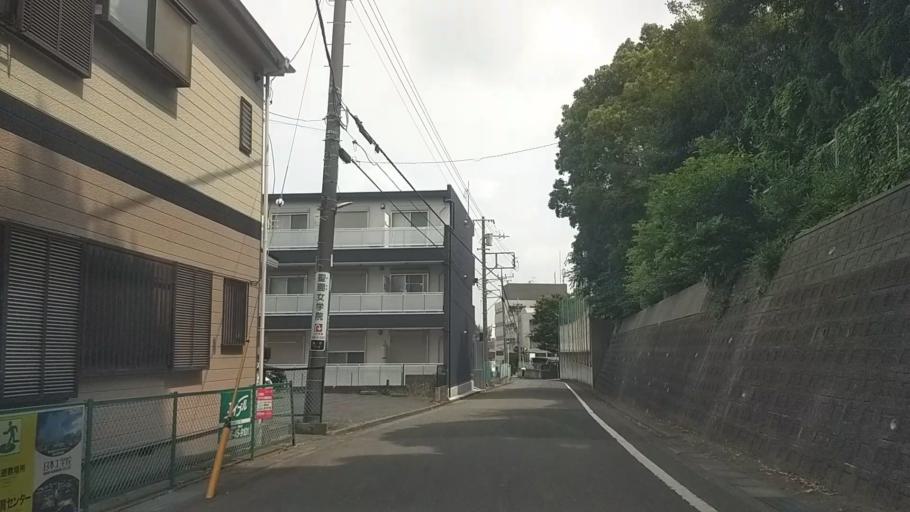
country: JP
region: Kanagawa
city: Fujisawa
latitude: 35.3612
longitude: 139.4737
